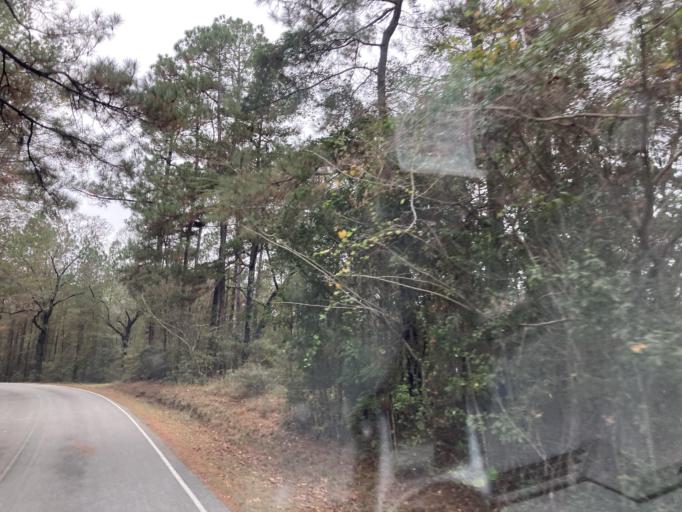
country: US
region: Mississippi
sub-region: Lamar County
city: Purvis
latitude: 31.2040
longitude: -89.4421
